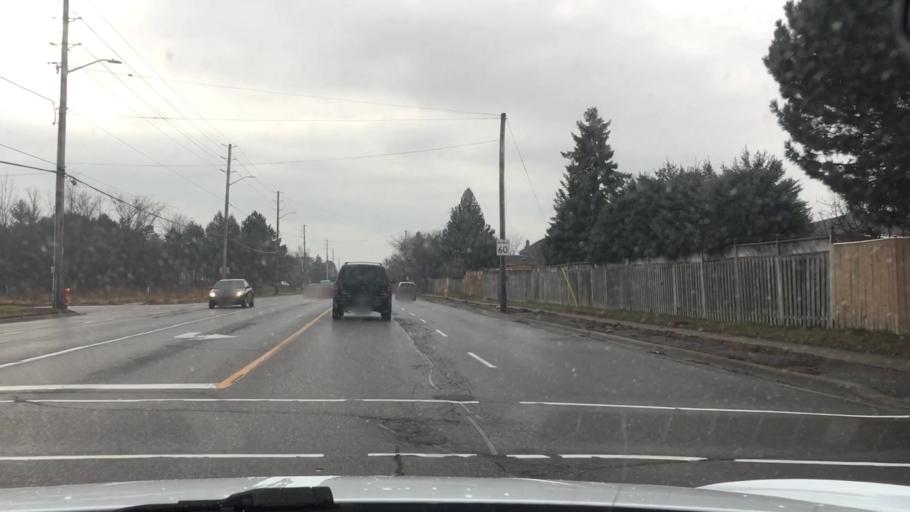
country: CA
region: Ontario
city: Oshawa
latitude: 43.9166
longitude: -78.8178
